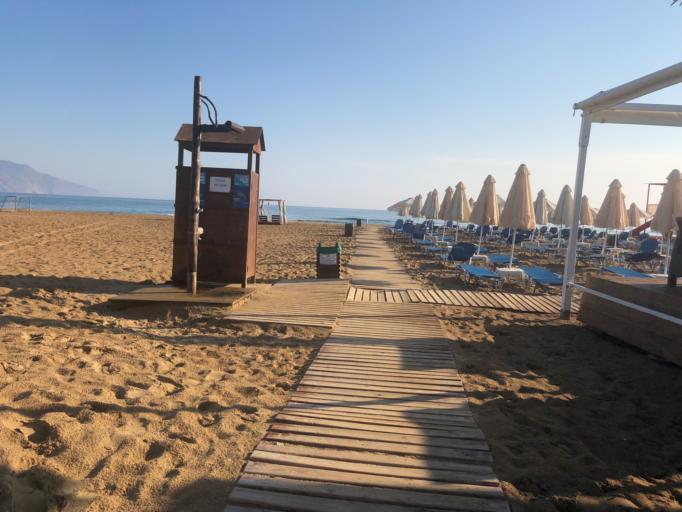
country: GR
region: Crete
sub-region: Nomos Chanias
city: Georgioupolis
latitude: 35.3549
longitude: 24.2861
